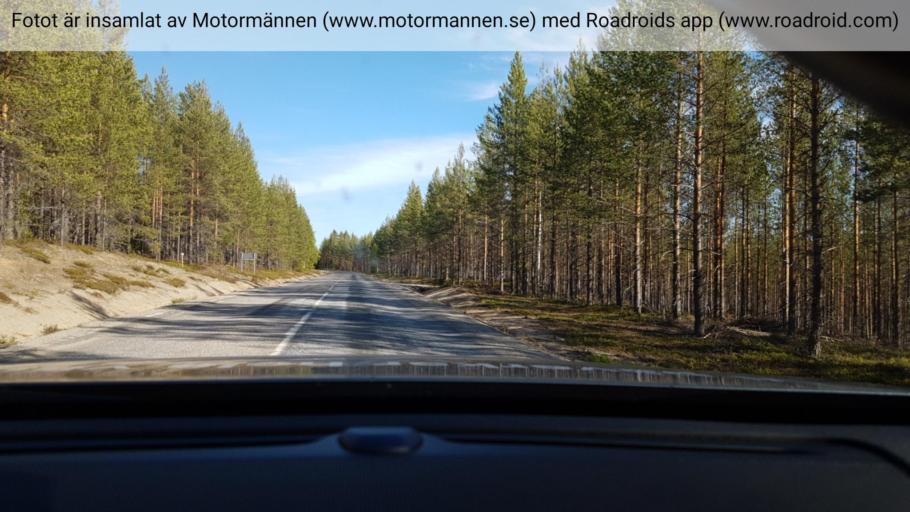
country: SE
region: Vaesterbotten
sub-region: Norsjo Kommun
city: Norsjoe
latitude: 64.7002
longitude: 19.1669
